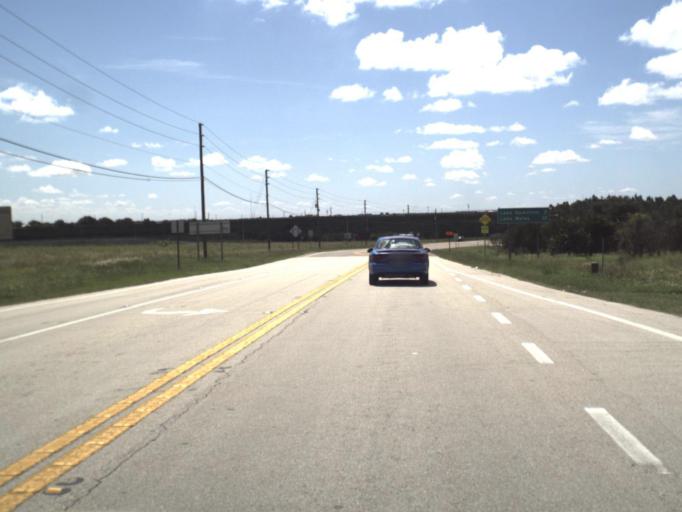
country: US
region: Florida
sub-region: Polk County
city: Haines City
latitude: 28.0841
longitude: -81.6215
